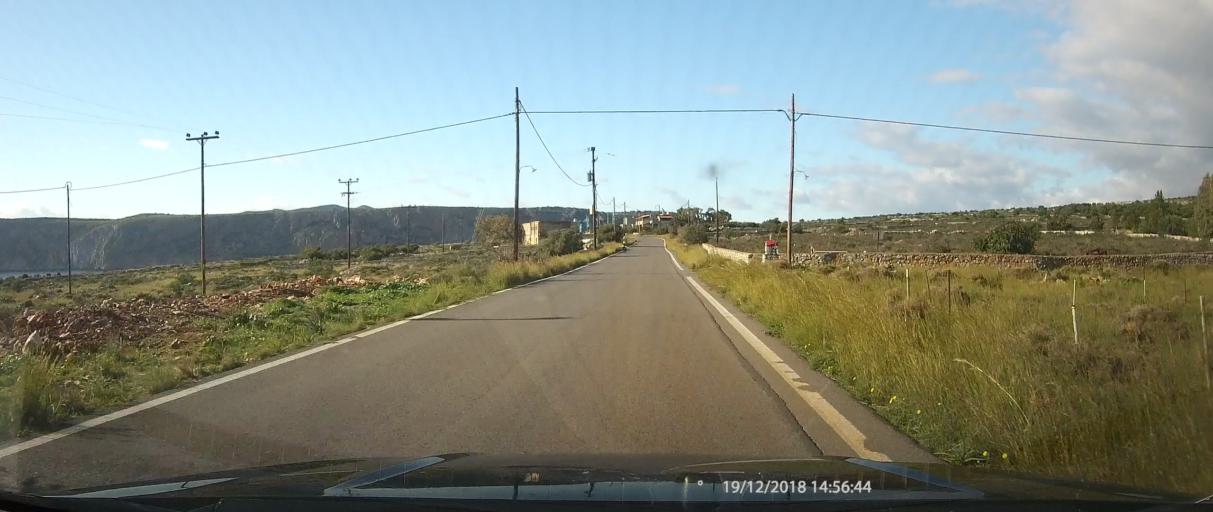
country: GR
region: Peloponnese
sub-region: Nomos Lakonias
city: Gytheio
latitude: 36.4779
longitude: 22.4135
